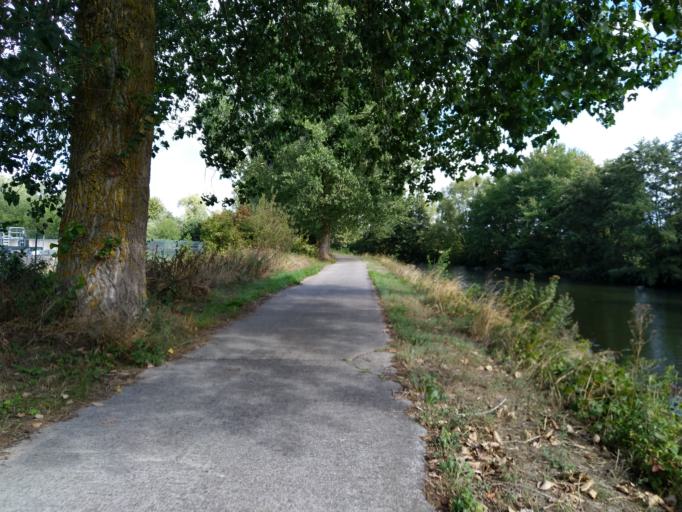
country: BE
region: Wallonia
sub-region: Province du Hainaut
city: Merbes-le-Chateau
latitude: 50.3125
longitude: 4.1504
